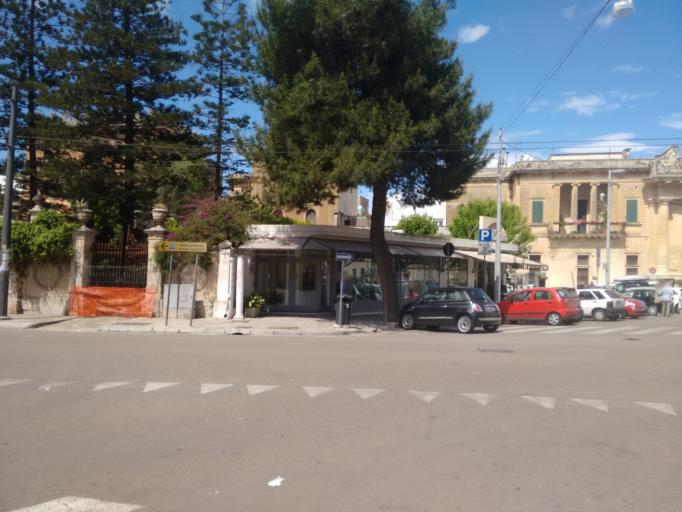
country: IT
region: Apulia
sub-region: Provincia di Lecce
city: Lecce
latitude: 40.3490
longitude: 18.1729
